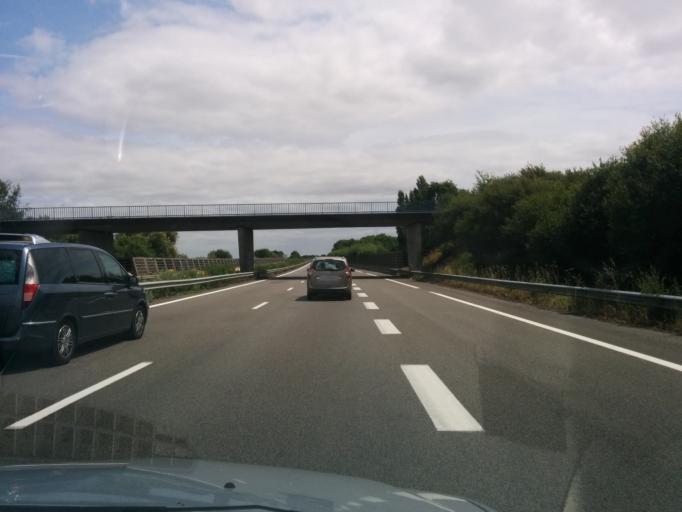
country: FR
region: Pays de la Loire
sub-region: Departement de la Loire-Atlantique
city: La Haie-Fouassiere
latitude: 47.1725
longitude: -1.3930
